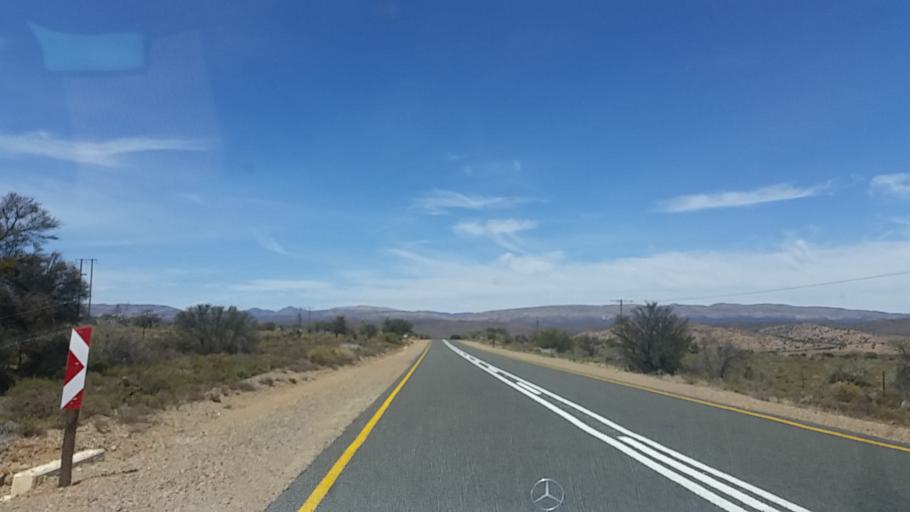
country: ZA
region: Eastern Cape
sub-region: Cacadu District Municipality
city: Willowmore
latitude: -33.4304
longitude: 23.3068
